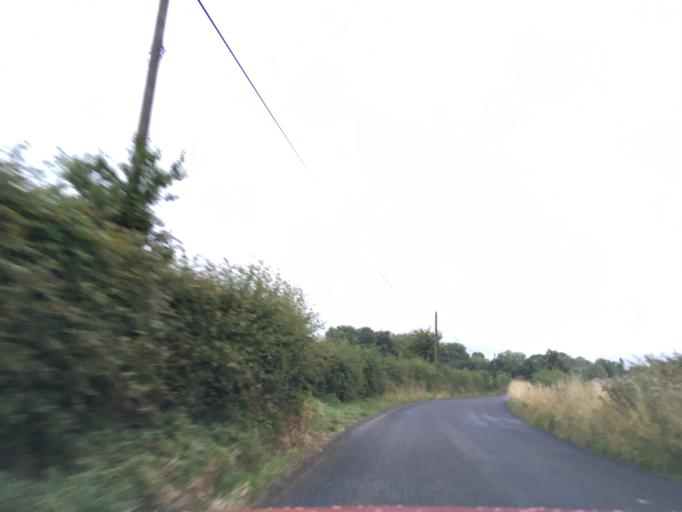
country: IE
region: Munster
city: Cahir
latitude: 52.4595
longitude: -7.9711
